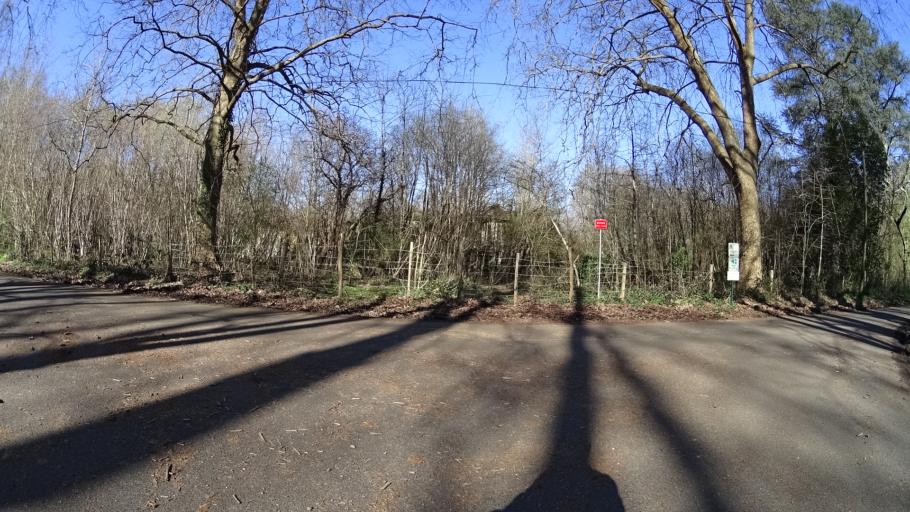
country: FR
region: Aquitaine
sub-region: Departement des Landes
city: Mees
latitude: 43.7490
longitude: -1.0947
